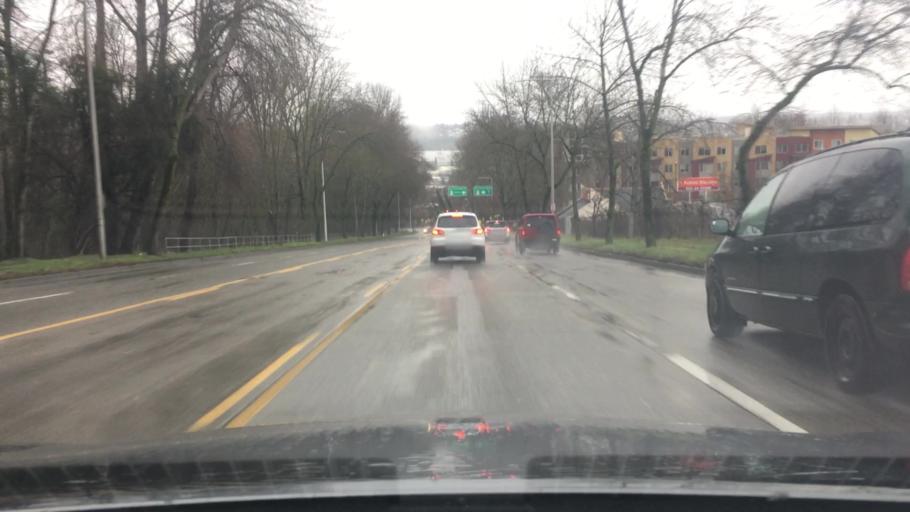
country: US
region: Washington
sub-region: King County
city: White Center
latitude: 47.5203
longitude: -122.3375
